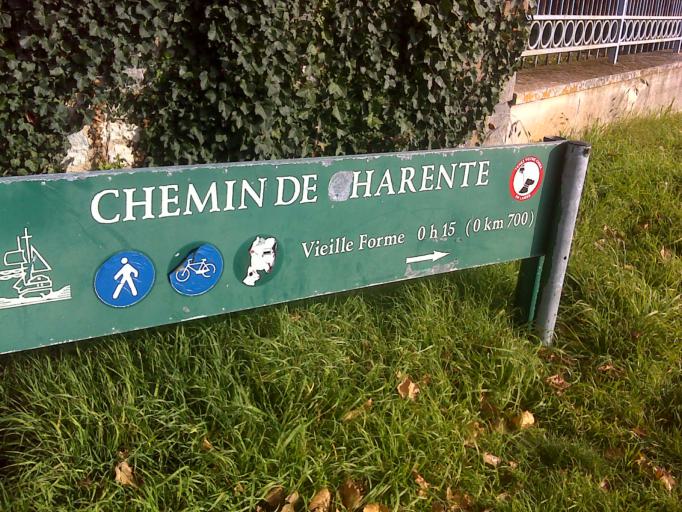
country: FR
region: Poitou-Charentes
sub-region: Departement de la Charente-Maritime
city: Rochefort
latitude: 45.9426
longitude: -0.9544
